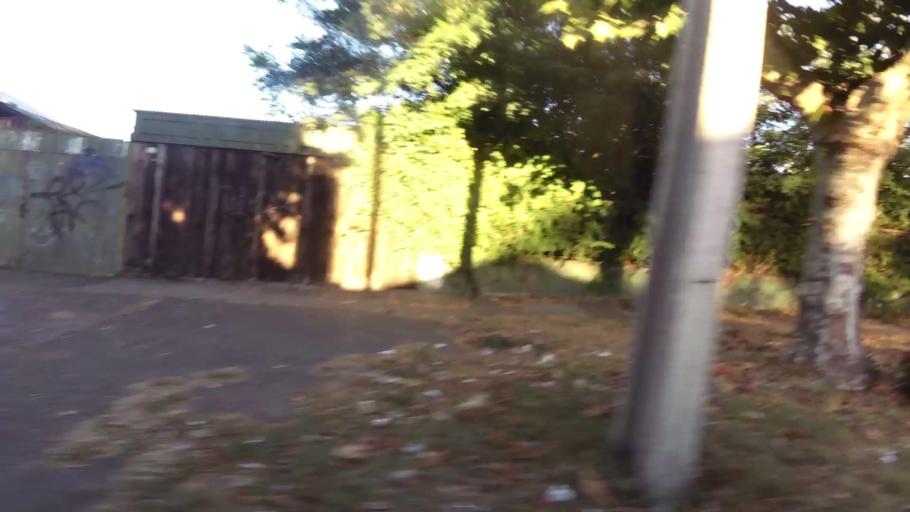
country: CL
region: Maule
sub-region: Provincia de Curico
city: Curico
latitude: -34.9926
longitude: -71.2390
